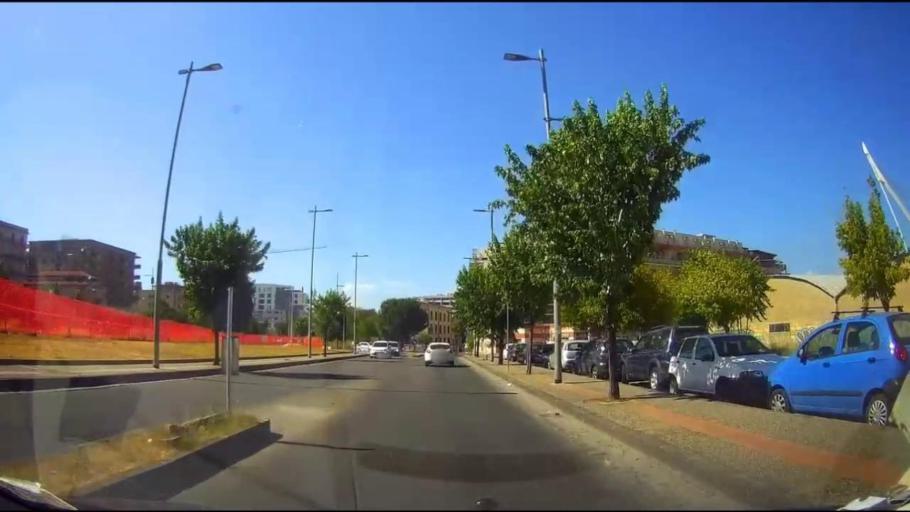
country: IT
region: Calabria
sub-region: Provincia di Cosenza
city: Cosenza
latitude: 39.2964
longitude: 16.2574
